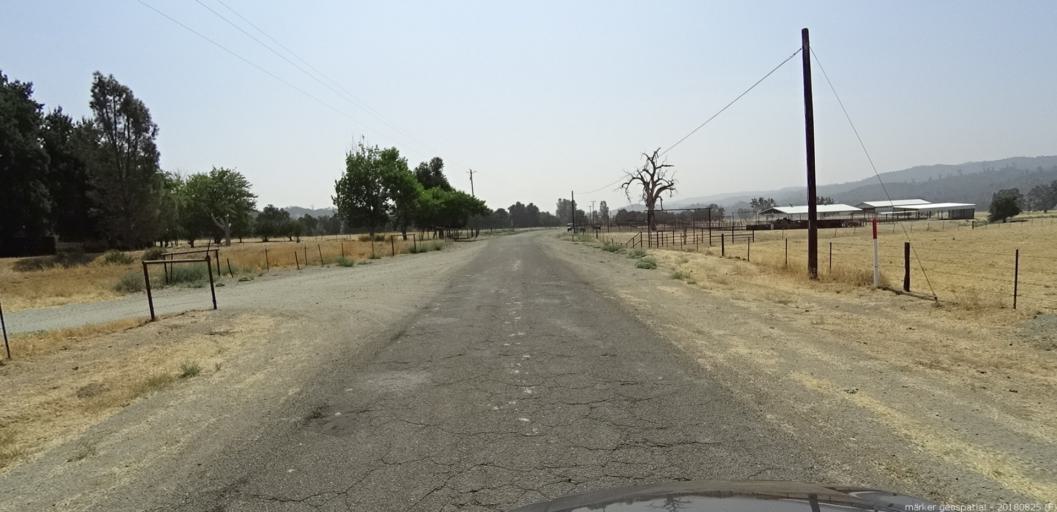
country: US
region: California
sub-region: Fresno County
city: Coalinga
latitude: 35.9459
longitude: -120.5250
